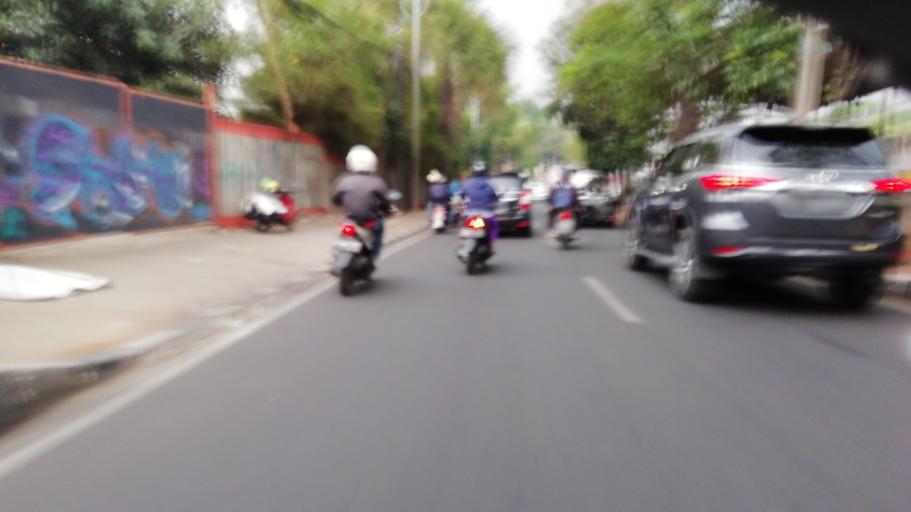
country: ID
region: Jakarta Raya
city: Jakarta
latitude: -6.2923
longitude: 106.8189
